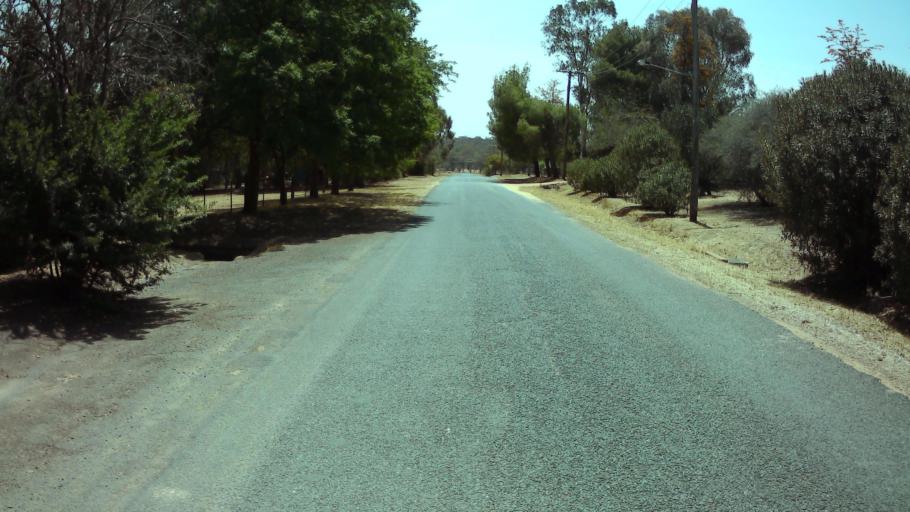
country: AU
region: New South Wales
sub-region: Weddin
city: Grenfell
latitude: -33.8955
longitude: 148.1721
